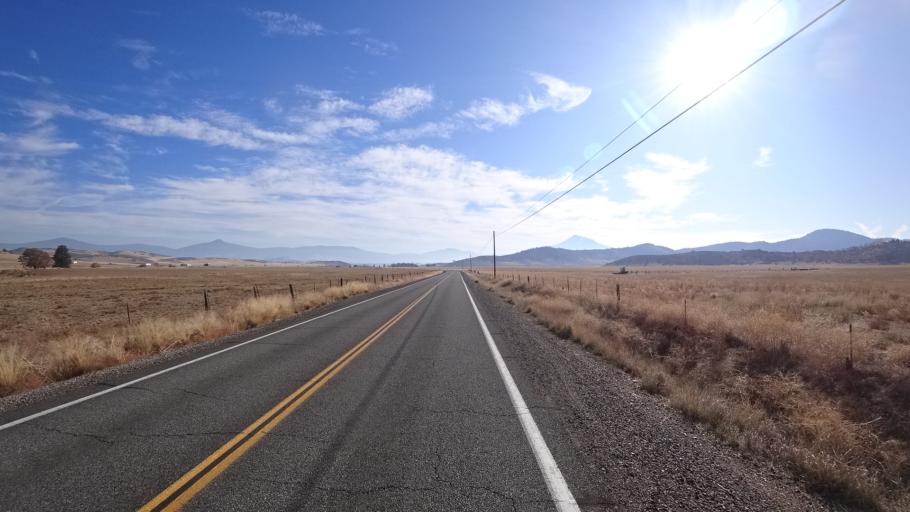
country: US
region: California
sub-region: Siskiyou County
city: Montague
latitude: 41.6555
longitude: -122.5795
